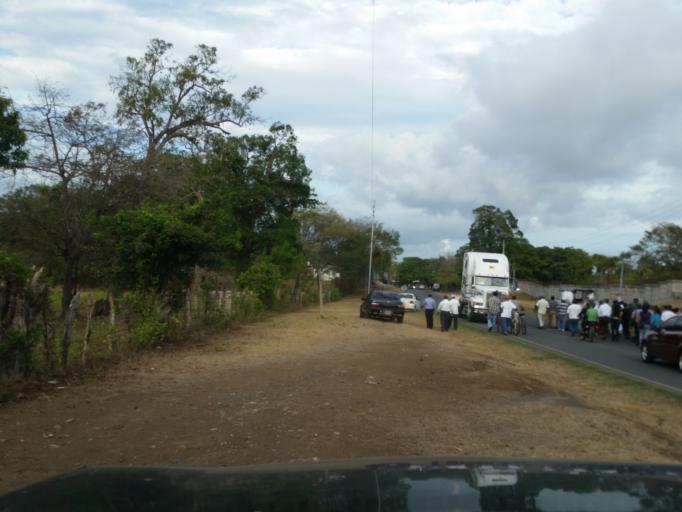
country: NI
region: Rivas
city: Rivas
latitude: 11.4413
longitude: -85.8418
